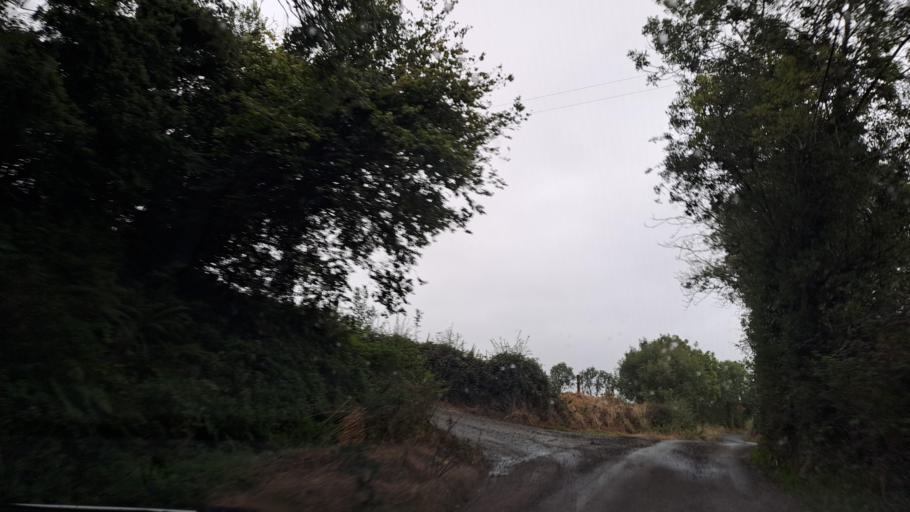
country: IE
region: Ulster
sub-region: An Cabhan
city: Kingscourt
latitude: 54.0038
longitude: -6.8420
